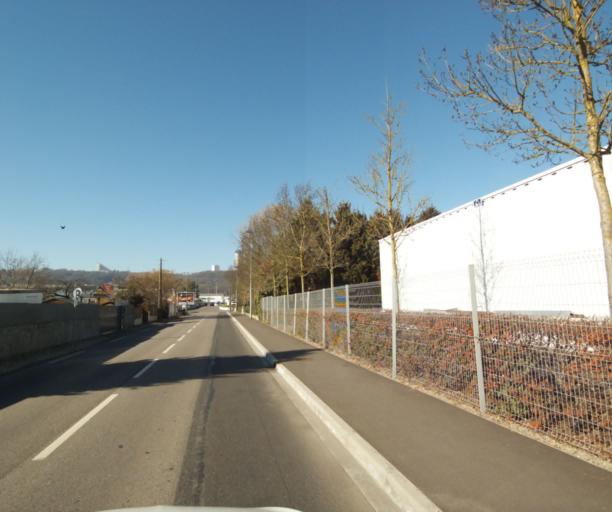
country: FR
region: Lorraine
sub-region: Departement de Meurthe-et-Moselle
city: Malzeville
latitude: 48.7105
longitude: 6.1758
